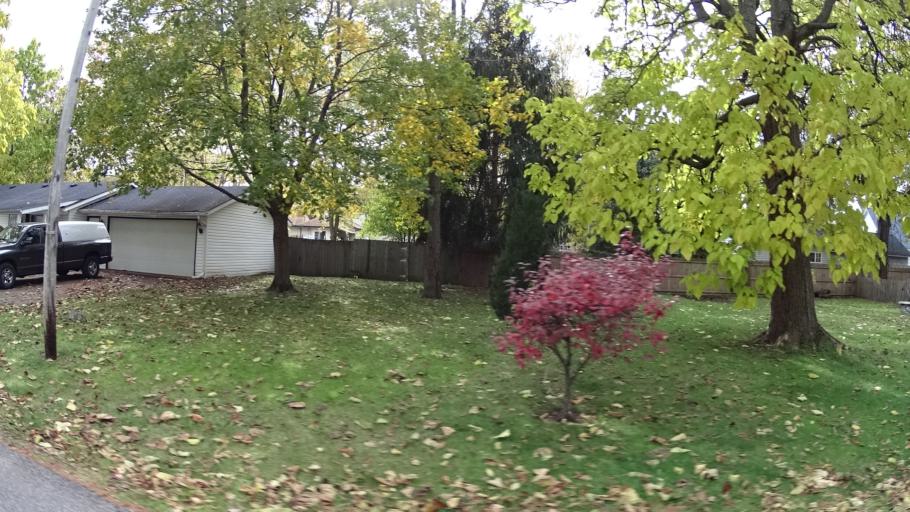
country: US
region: Ohio
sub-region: Lorain County
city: Sheffield
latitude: 41.4223
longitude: -82.1258
